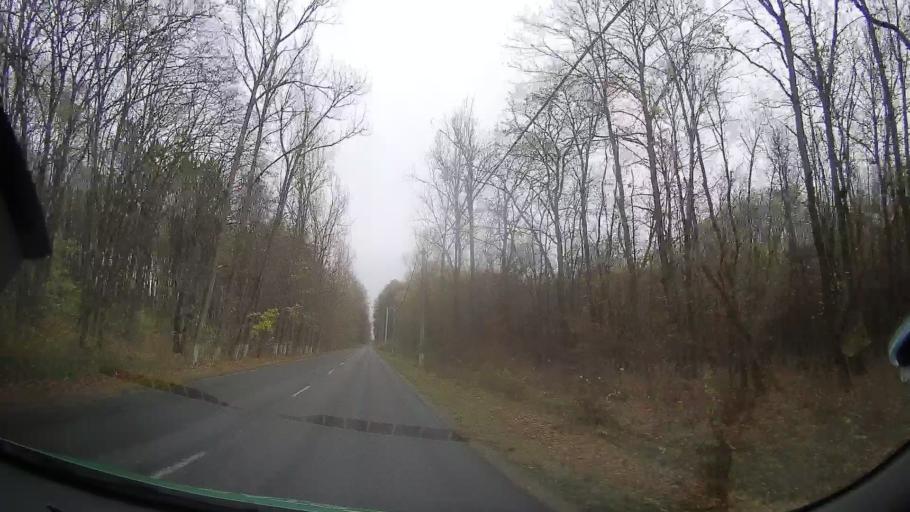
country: RO
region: Ilfov
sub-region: Comuna Snagov
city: Snagov
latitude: 44.7165
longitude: 26.1986
